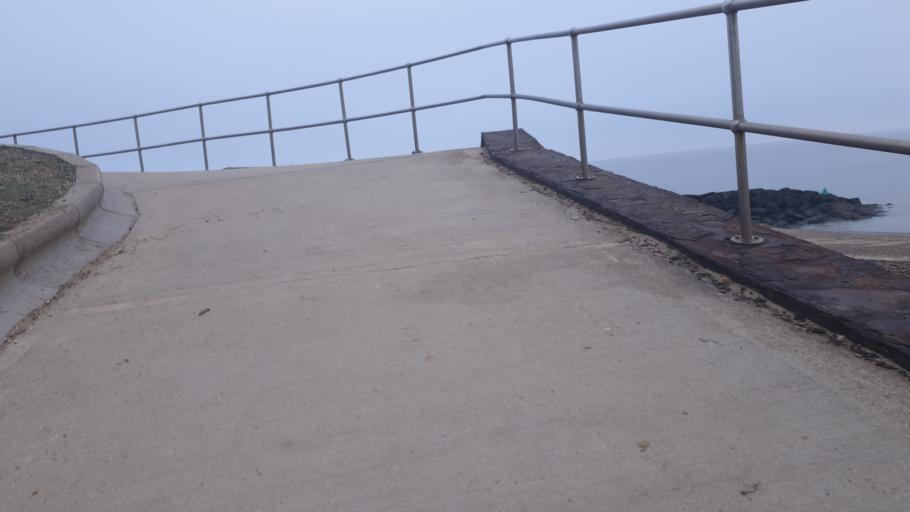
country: GB
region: England
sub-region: Essex
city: Clacton-on-Sea
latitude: 51.7963
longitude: 1.1805
